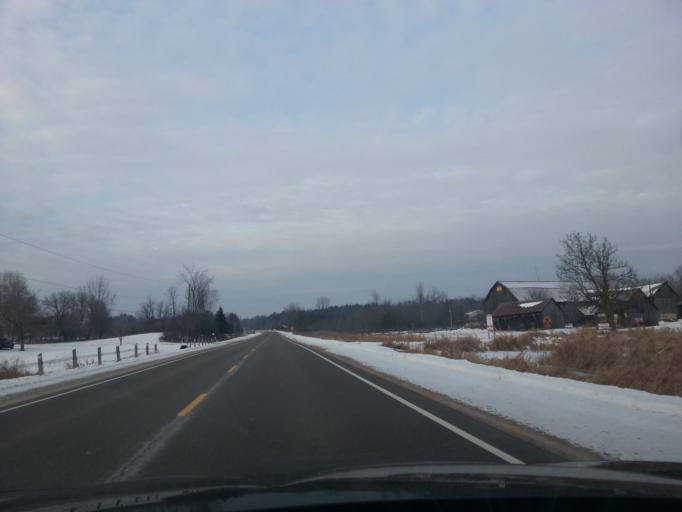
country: CA
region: Ontario
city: Perth
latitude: 44.8620
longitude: -76.4186
